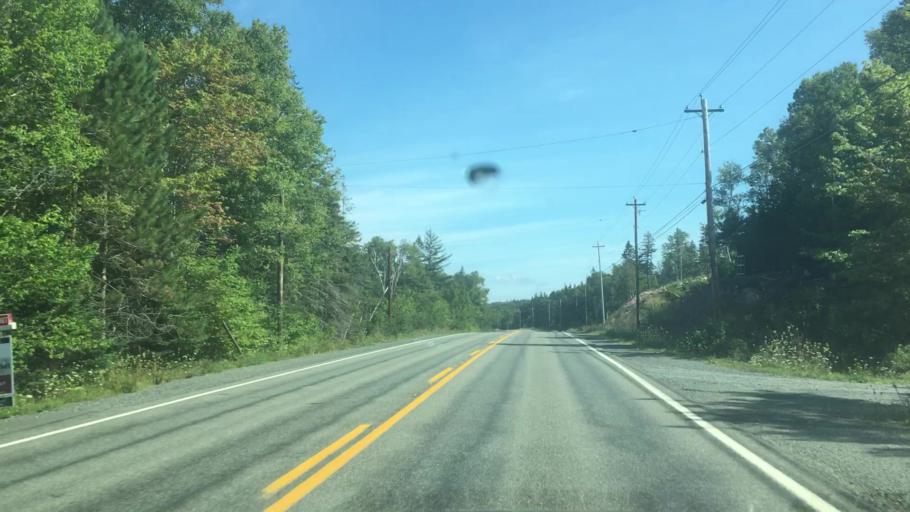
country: CA
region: Nova Scotia
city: Sydney
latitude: 45.9881
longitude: -60.4160
